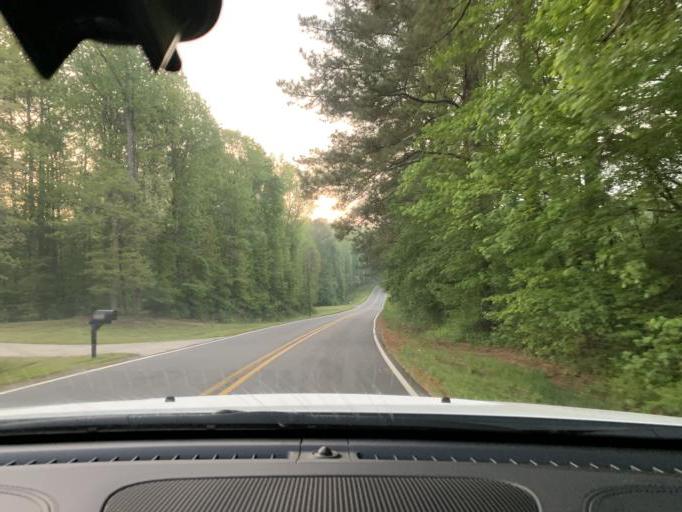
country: US
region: Georgia
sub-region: Dawson County
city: Dawsonville
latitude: 34.3283
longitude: -84.1745
